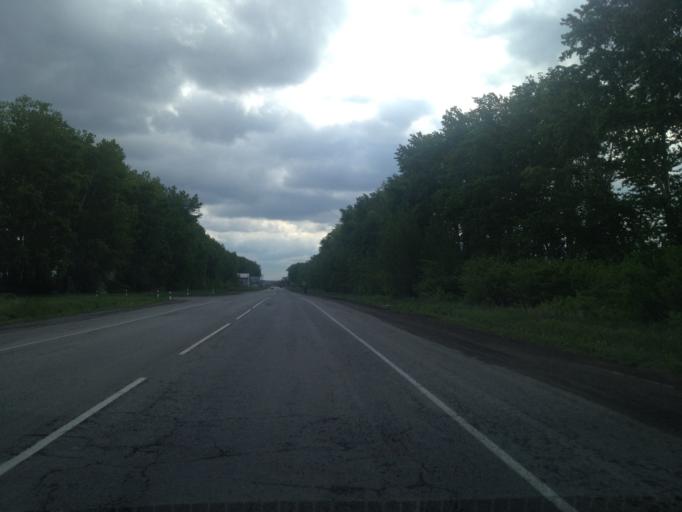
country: RU
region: Sverdlovsk
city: Aramil
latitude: 56.6948
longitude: 60.7770
